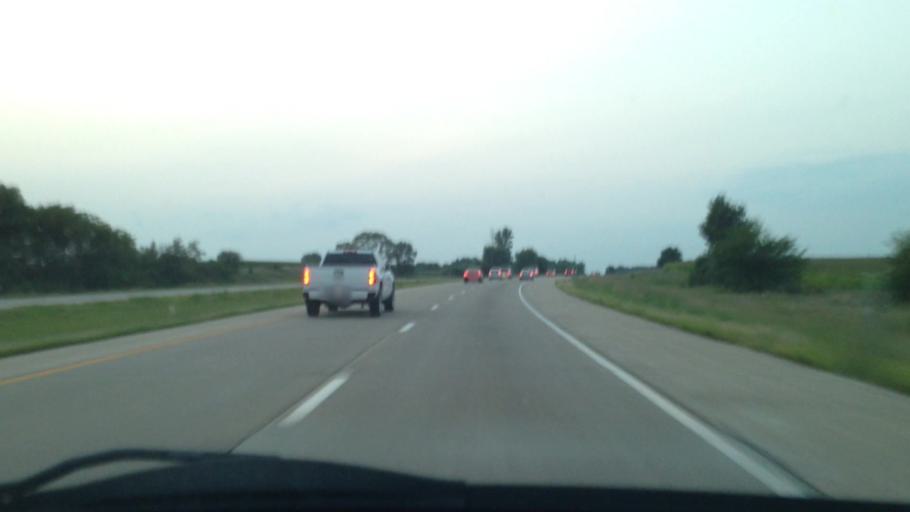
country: US
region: Iowa
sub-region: Black Hawk County
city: Elk Run Heights
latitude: 42.4234
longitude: -92.1848
